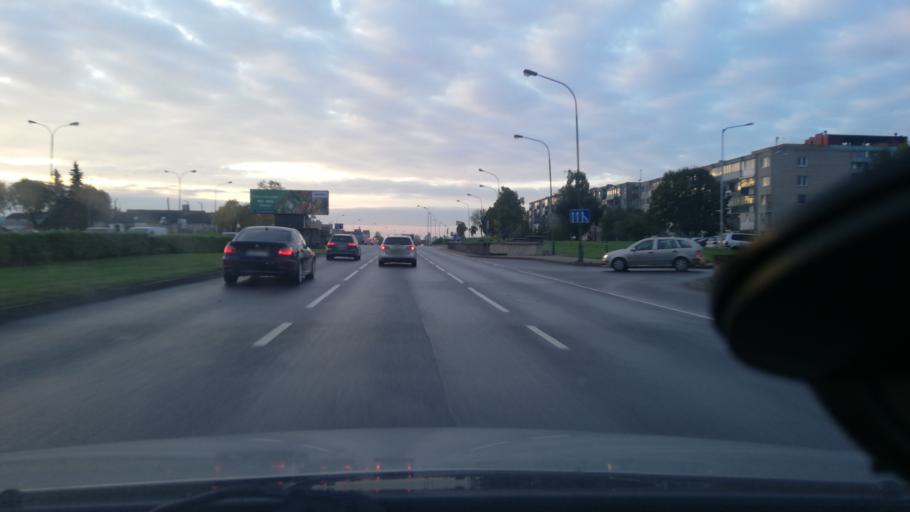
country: LT
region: Klaipedos apskritis
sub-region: Klaipeda
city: Klaipeda
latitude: 55.6894
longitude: 21.1806
